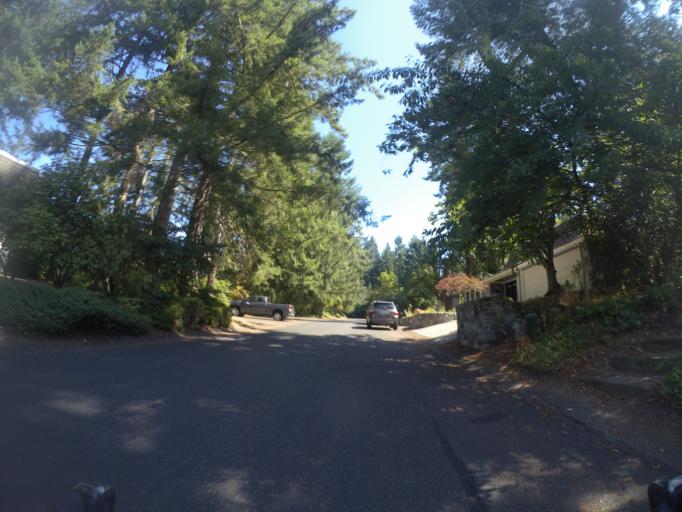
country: US
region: Washington
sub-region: Pierce County
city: University Place
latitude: 47.2138
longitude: -122.5648
